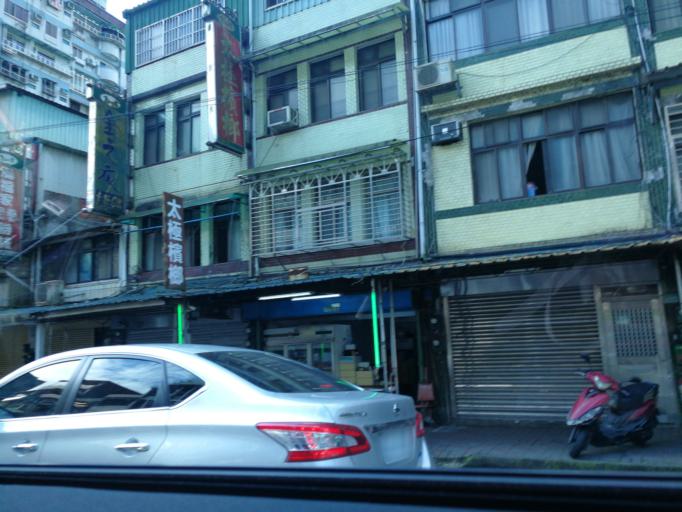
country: TW
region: Taipei
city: Taipei
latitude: 24.9522
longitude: 121.5473
